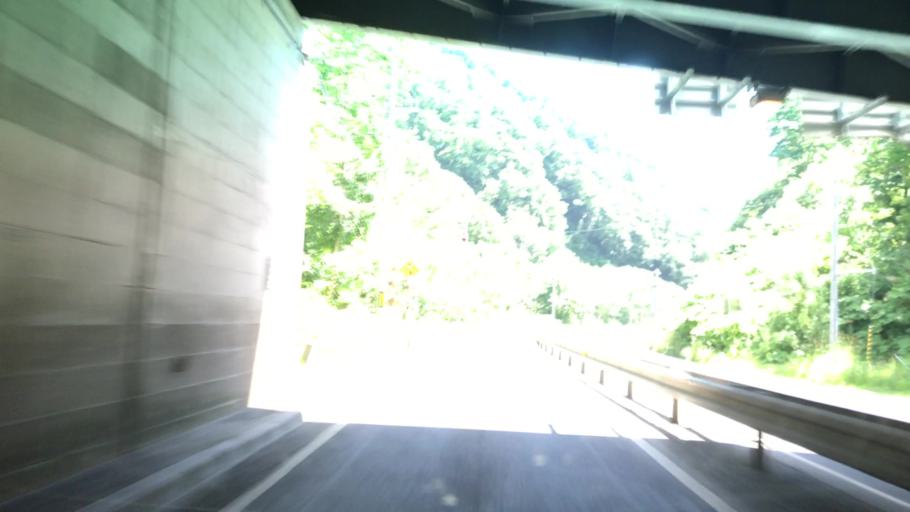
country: JP
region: Hokkaido
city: Yoichi
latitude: 43.0454
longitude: 140.6813
